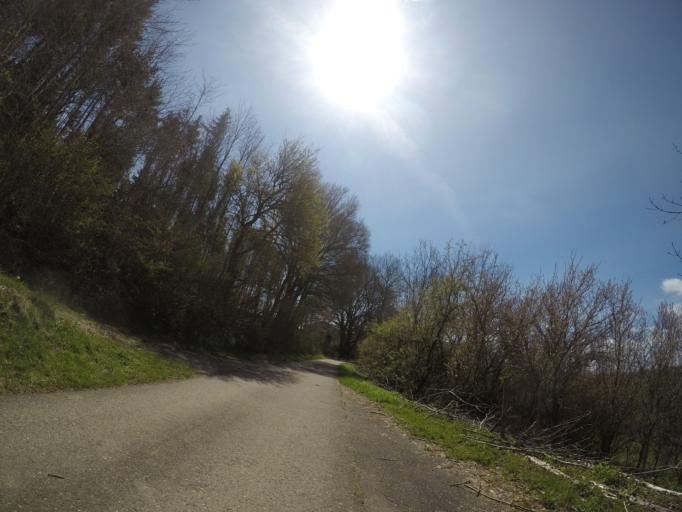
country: DE
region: Baden-Wuerttemberg
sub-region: Regierungsbezirk Stuttgart
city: Neidlingen
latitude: 48.5255
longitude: 9.5668
